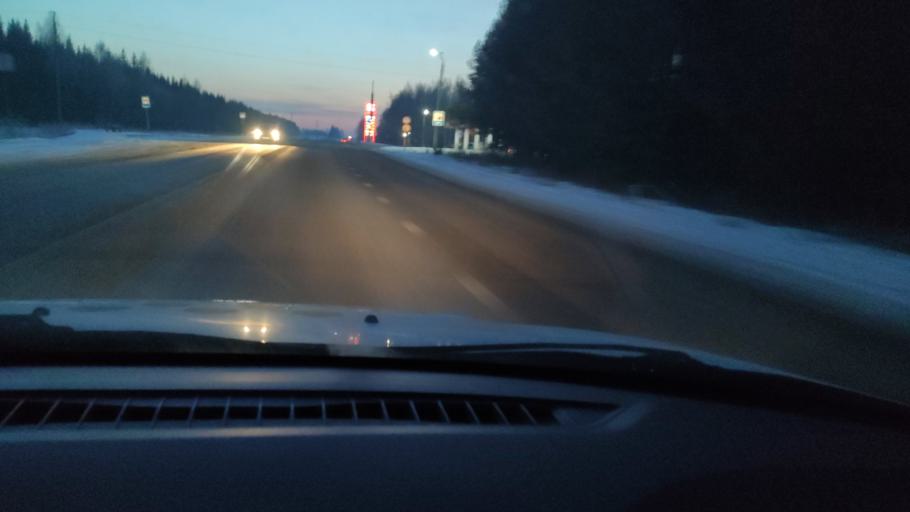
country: RU
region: Perm
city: Kungur
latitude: 57.4108
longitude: 56.9079
